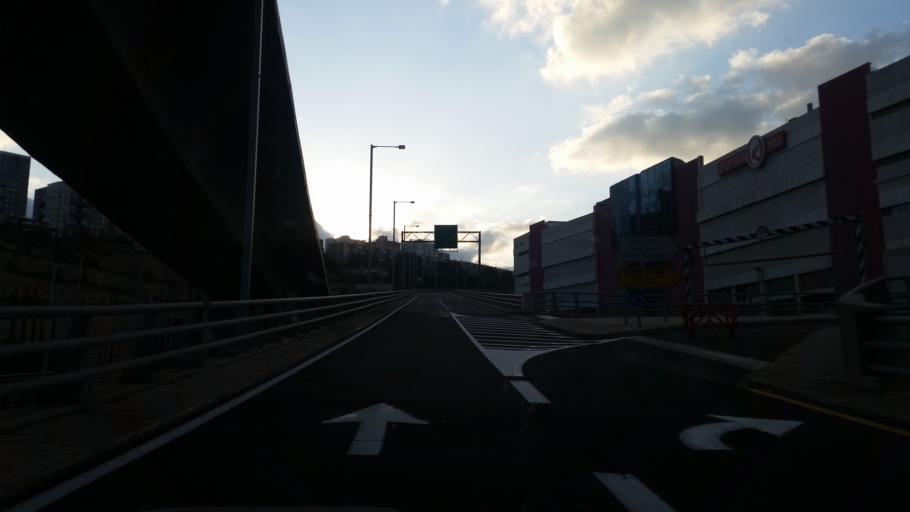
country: IL
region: Haifa
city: Haifa
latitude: 32.7906
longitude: 35.0065
